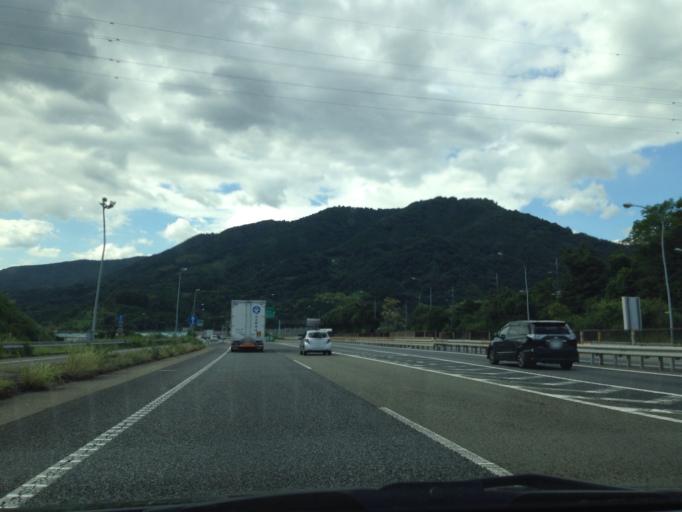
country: JP
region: Kanagawa
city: Hadano
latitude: 35.3440
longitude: 139.1558
